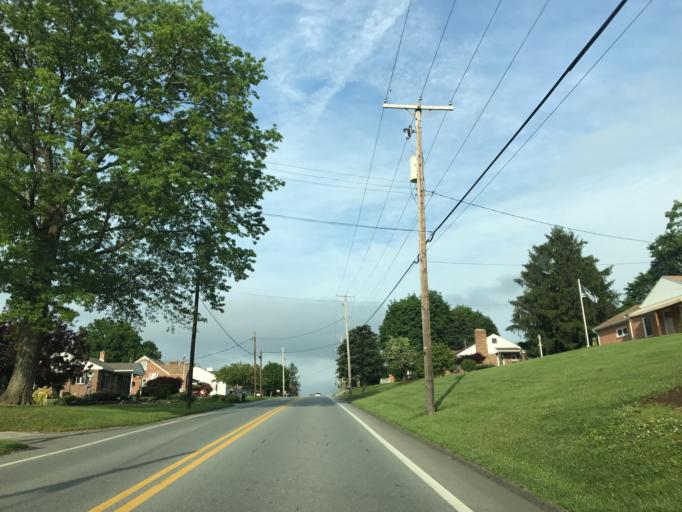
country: US
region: Pennsylvania
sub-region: York County
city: Stonybrook
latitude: 39.9606
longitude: -76.6466
